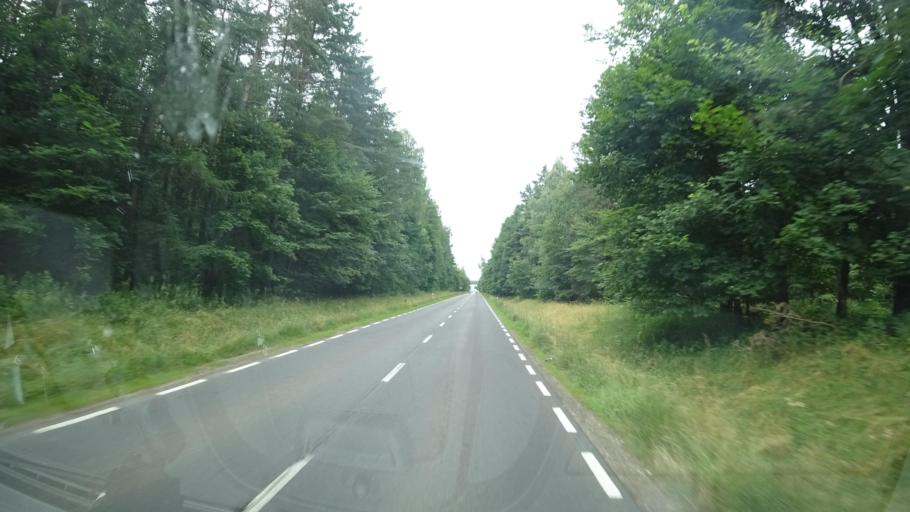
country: PL
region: Warmian-Masurian Voivodeship
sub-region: Powiat goldapski
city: Goldap
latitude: 54.3283
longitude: 22.2972
